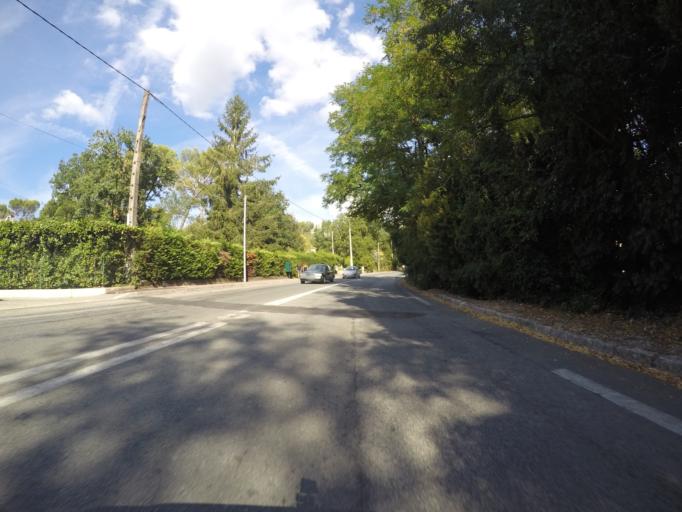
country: FR
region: Provence-Alpes-Cote d'Azur
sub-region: Departement des Alpes-Maritimes
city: Le Rouret
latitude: 43.6686
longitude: 7.0420
